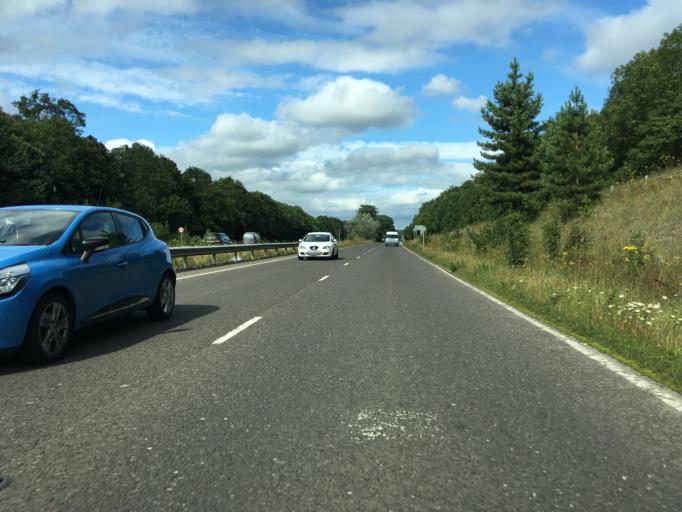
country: GB
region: England
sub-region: West Sussex
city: Horsham
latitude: 51.0709
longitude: -0.3501
